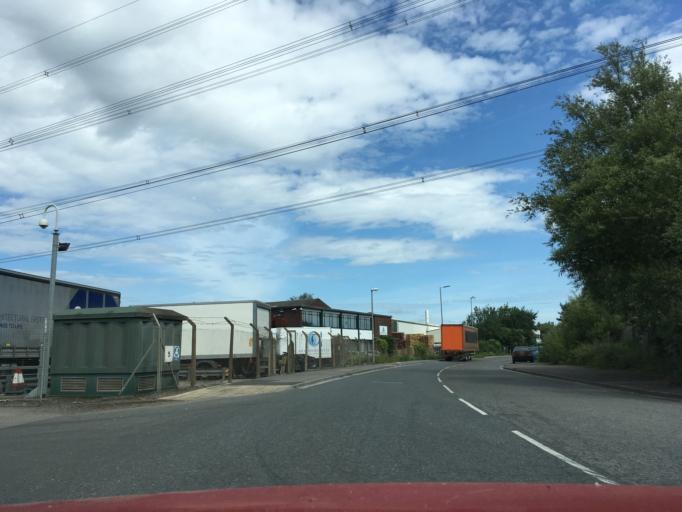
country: GB
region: Wales
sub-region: Newport
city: Nash
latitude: 51.5665
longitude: -2.9698
